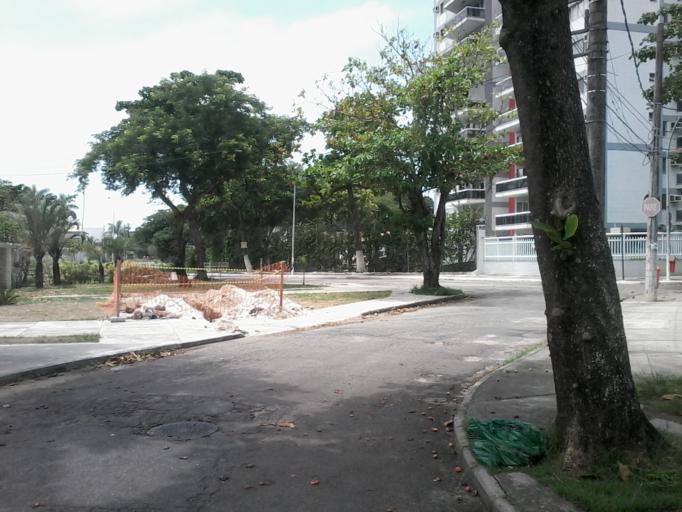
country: BR
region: Rio de Janeiro
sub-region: Nilopolis
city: Nilopolis
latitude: -23.0222
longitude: -43.4850
